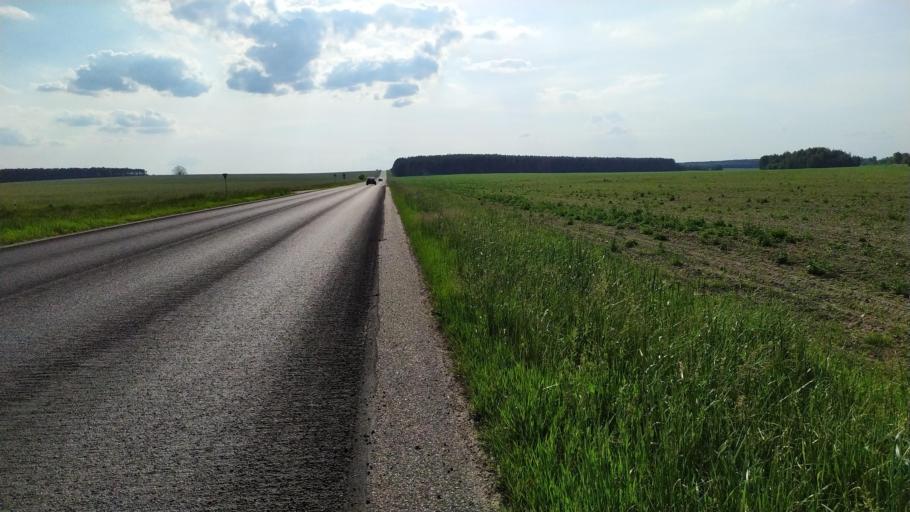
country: BY
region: Brest
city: Kamyanyets
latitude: 52.3927
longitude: 23.9735
